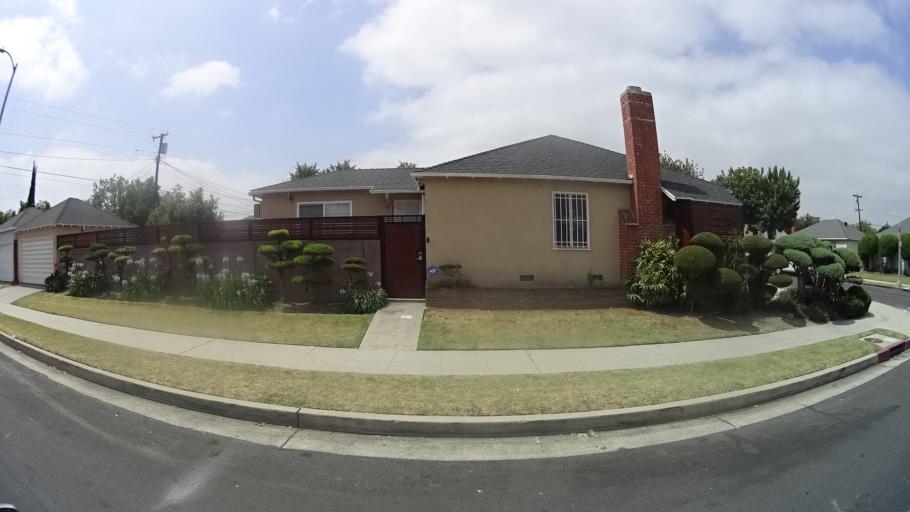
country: US
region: California
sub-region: Los Angeles County
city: View Park-Windsor Hills
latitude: 34.0182
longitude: -118.3421
